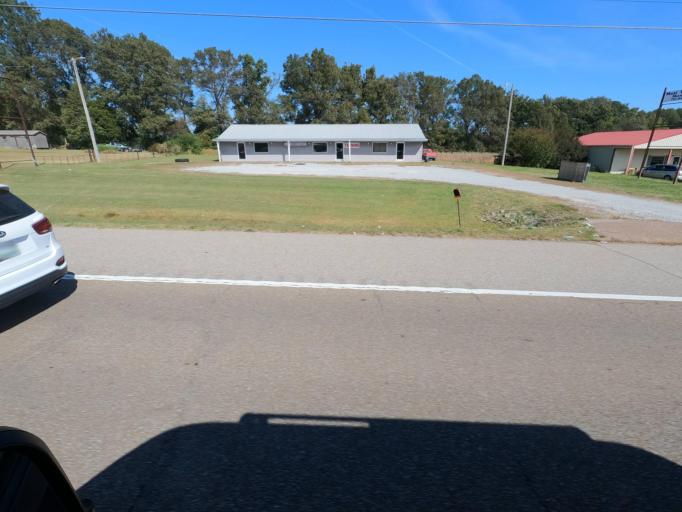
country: US
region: Tennessee
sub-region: Crockett County
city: Bells
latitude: 35.7411
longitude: -89.0867
